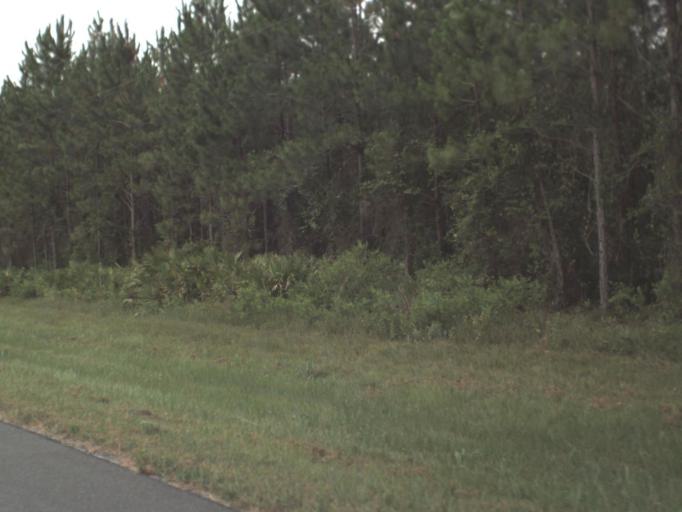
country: US
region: Florida
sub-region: Hamilton County
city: Jasper
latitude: 30.5132
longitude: -82.6699
